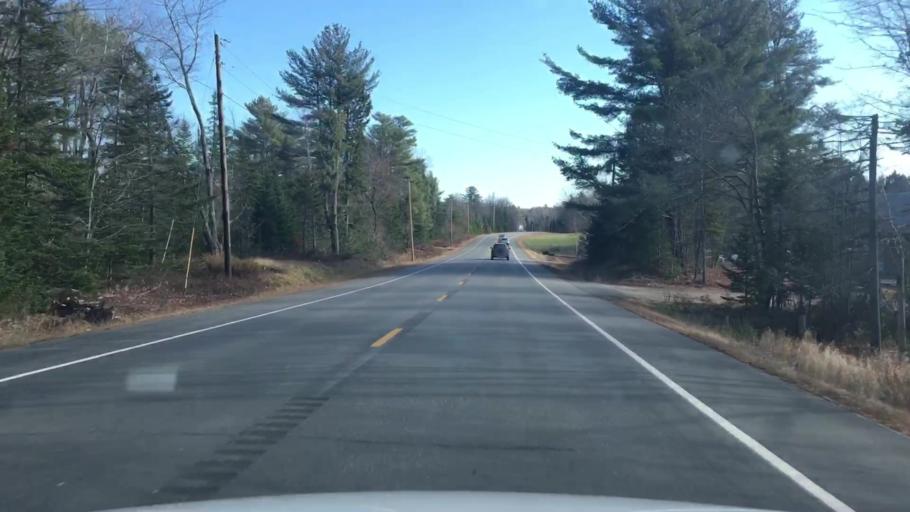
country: US
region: Maine
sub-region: Lincoln County
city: Jefferson
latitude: 44.2539
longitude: -69.4357
